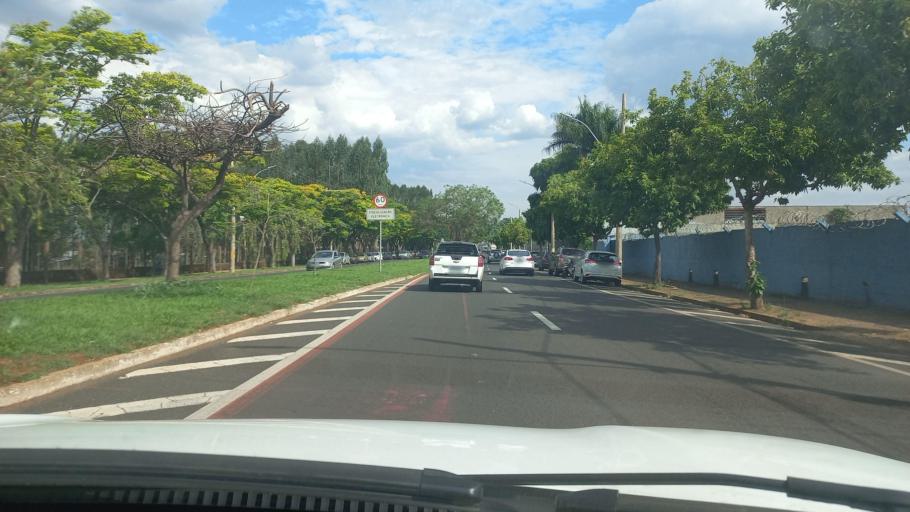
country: BR
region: Minas Gerais
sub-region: Uberaba
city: Uberaba
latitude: -19.7611
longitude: -47.9643
